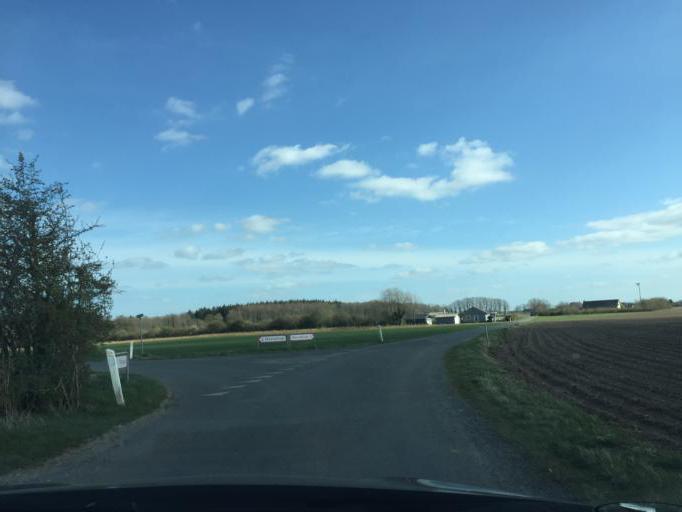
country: DK
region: South Denmark
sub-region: Kerteminde Kommune
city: Langeskov
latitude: 55.3058
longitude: 10.5458
